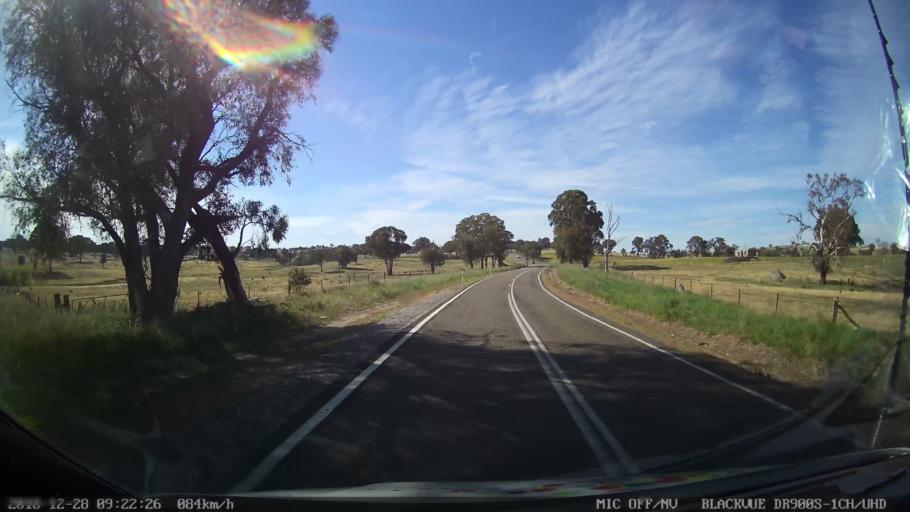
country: AU
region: New South Wales
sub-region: Upper Lachlan Shire
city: Crookwell
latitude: -34.3736
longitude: 149.3819
